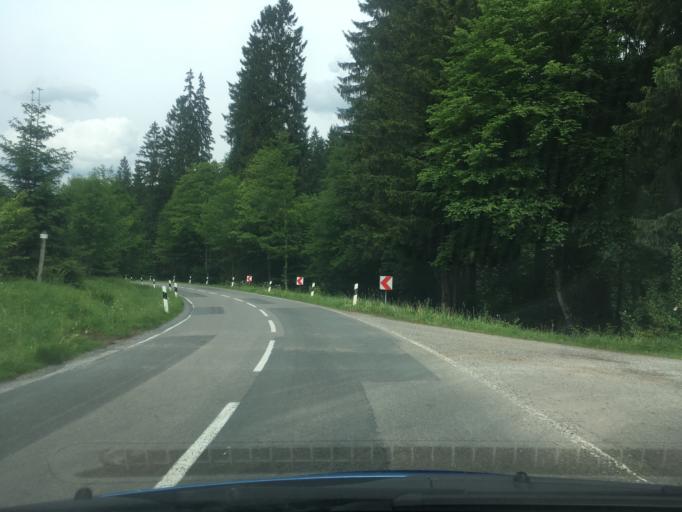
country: DE
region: Lower Saxony
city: Uslar
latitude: 51.7319
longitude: 9.6352
